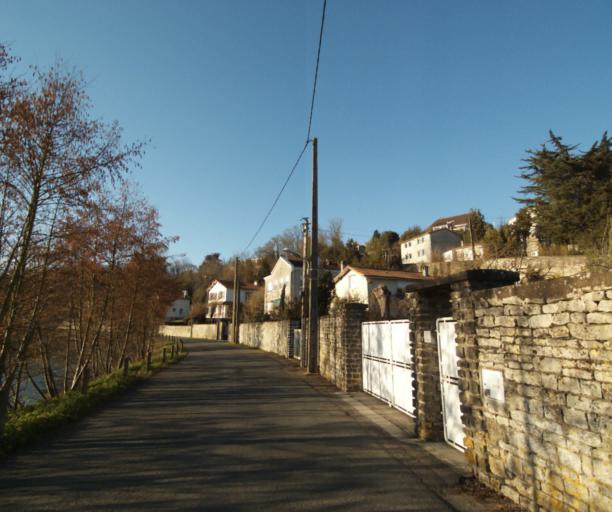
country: FR
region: Poitou-Charentes
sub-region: Departement des Deux-Sevres
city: Niort
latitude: 46.3356
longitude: -0.4793
